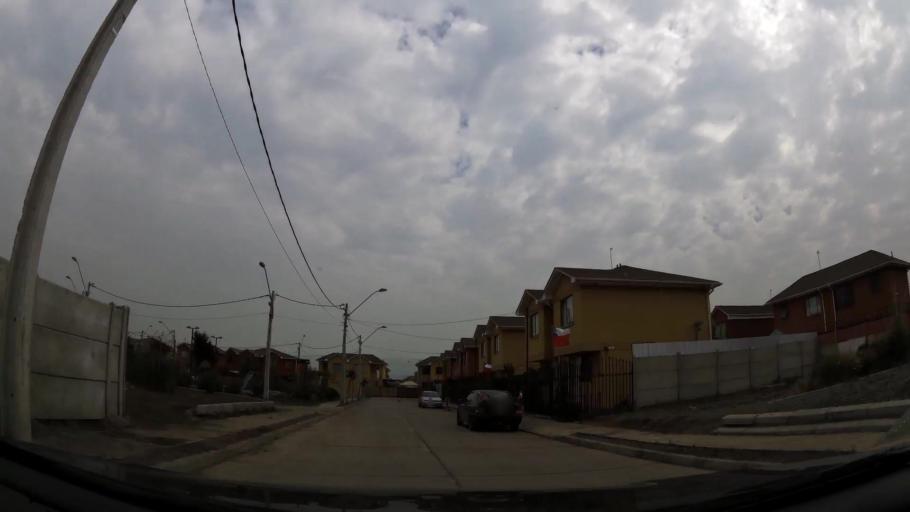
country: CL
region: Santiago Metropolitan
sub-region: Provincia de Chacabuco
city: Chicureo Abajo
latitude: -33.1927
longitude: -70.6780
